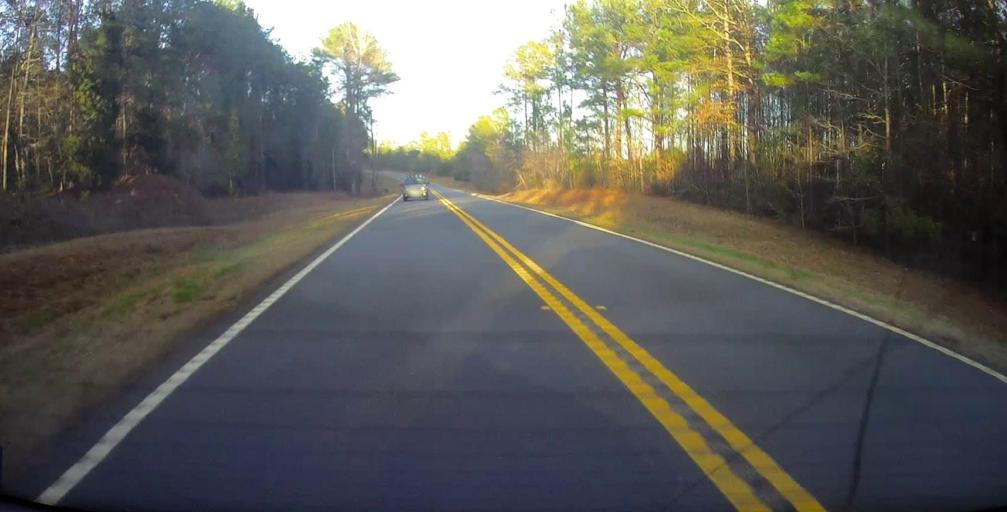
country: US
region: Georgia
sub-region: Talbot County
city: Sardis
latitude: 32.7273
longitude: -84.6256
